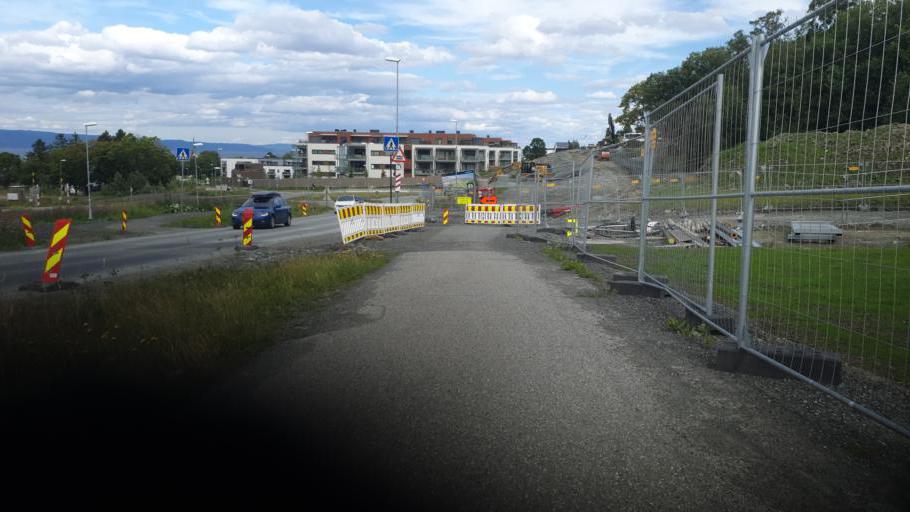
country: NO
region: Sor-Trondelag
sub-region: Klaebu
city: Klaebu
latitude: 63.4238
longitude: 10.5353
